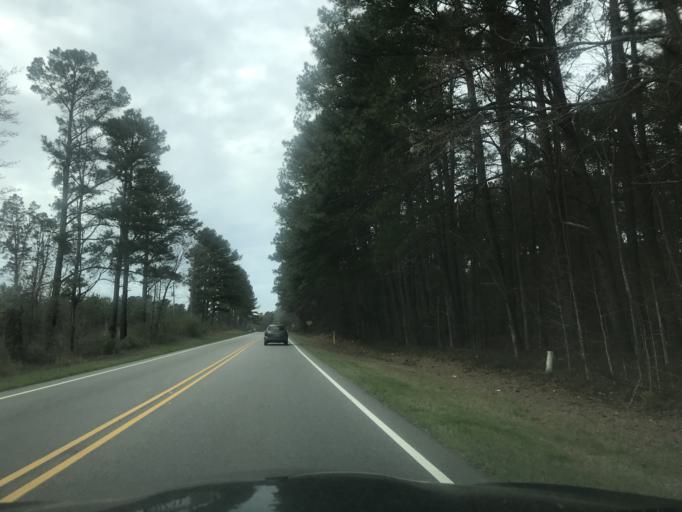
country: US
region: North Carolina
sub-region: Franklin County
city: Franklinton
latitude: 36.0993
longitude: -78.4246
